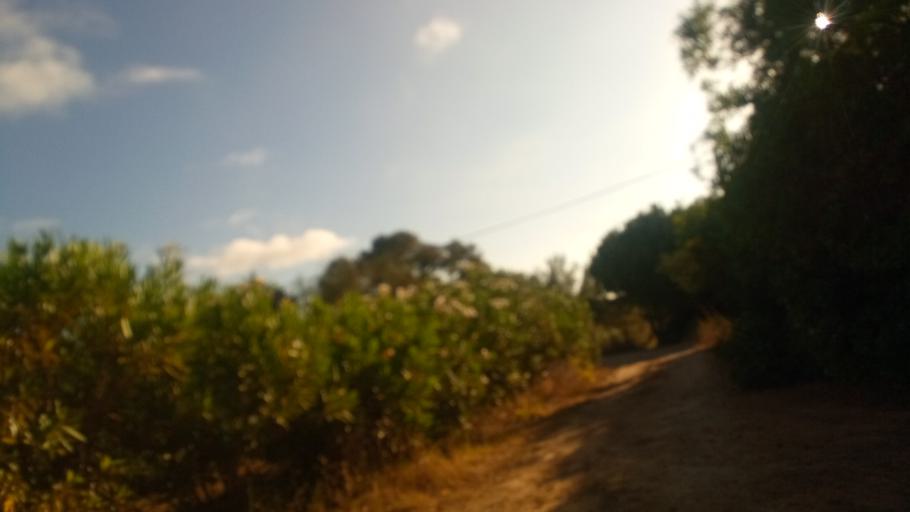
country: PT
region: Faro
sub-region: Tavira
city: Tavira
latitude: 37.1436
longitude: -7.5830
